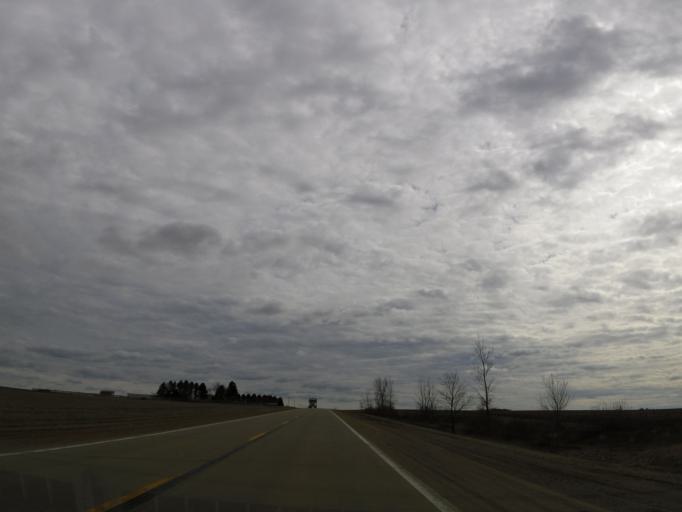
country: US
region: Iowa
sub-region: Howard County
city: Cresco
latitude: 43.3850
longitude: -92.2982
